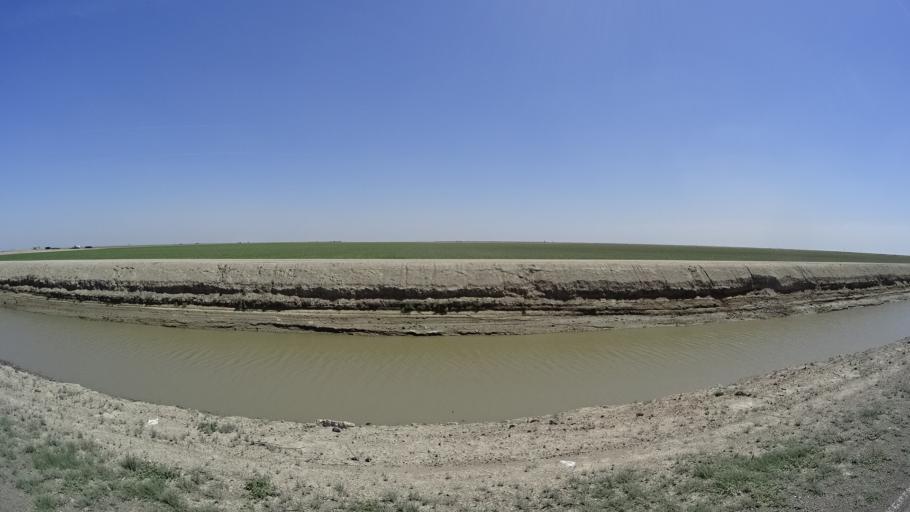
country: US
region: California
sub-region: Kings County
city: Corcoran
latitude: 35.9605
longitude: -119.6452
